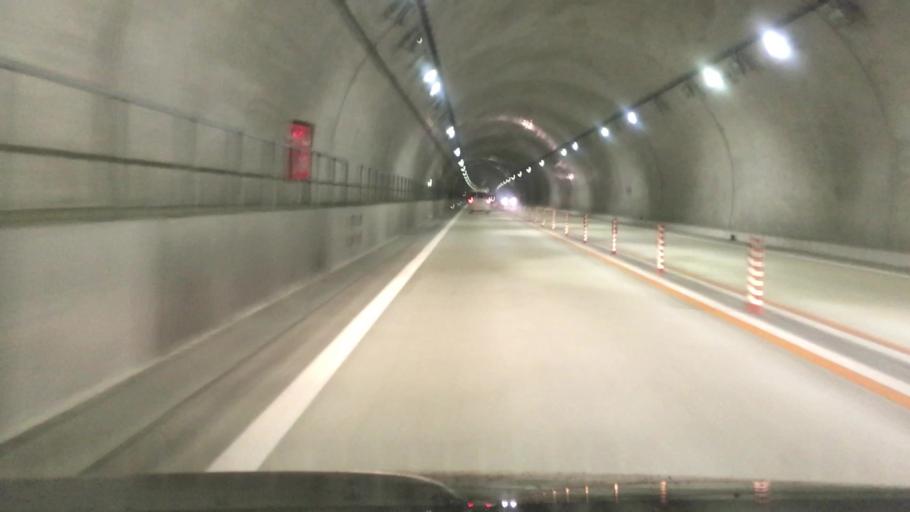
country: JP
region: Hyogo
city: Toyooka
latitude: 35.4510
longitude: 134.7654
